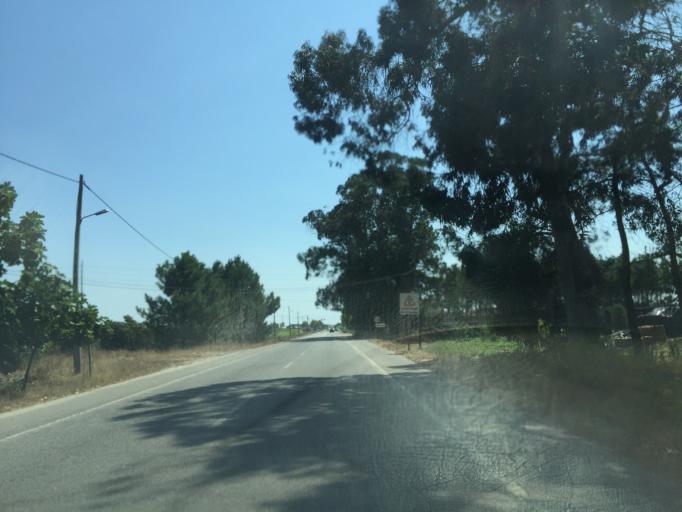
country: PT
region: Coimbra
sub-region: Mira
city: Mira
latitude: 40.3316
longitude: -8.7510
